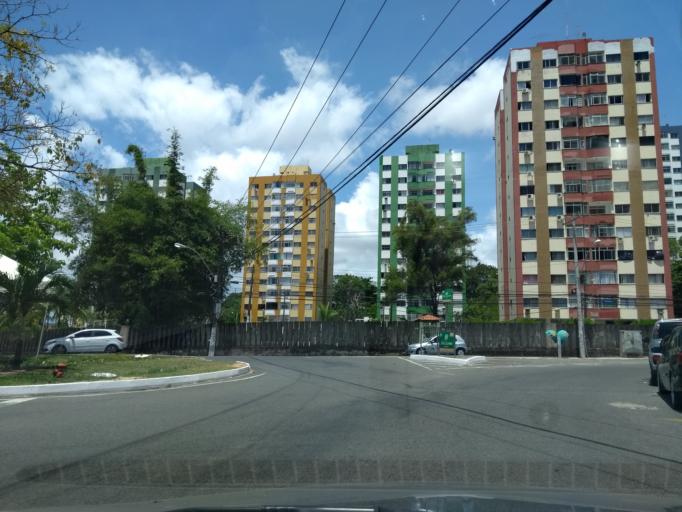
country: BR
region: Bahia
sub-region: Salvador
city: Salvador
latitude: -12.9685
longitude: -38.4354
